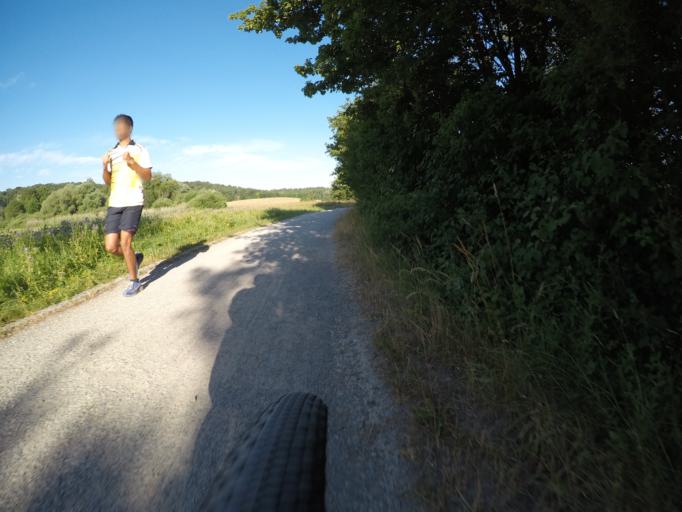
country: DE
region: Baden-Wuerttemberg
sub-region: Regierungsbezirk Stuttgart
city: Gerlingen
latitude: 48.7453
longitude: 9.0912
